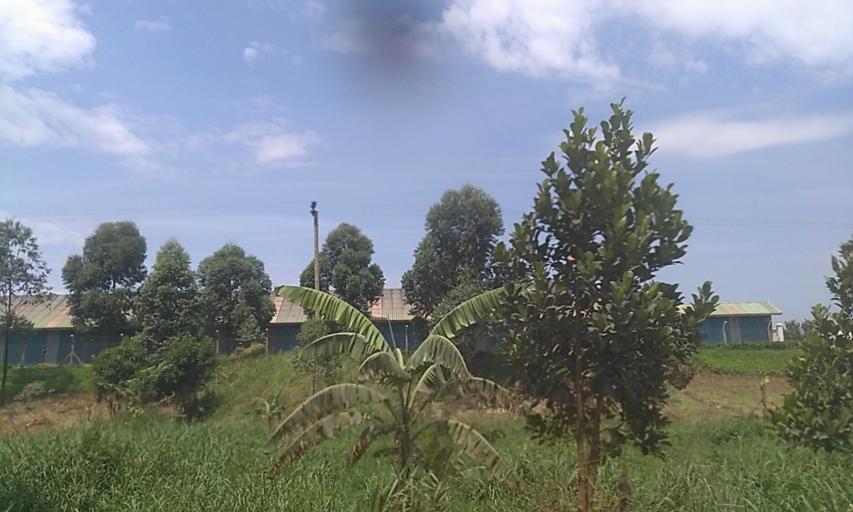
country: UG
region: Central Region
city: Kampala Central Division
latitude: 0.3464
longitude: 32.5478
